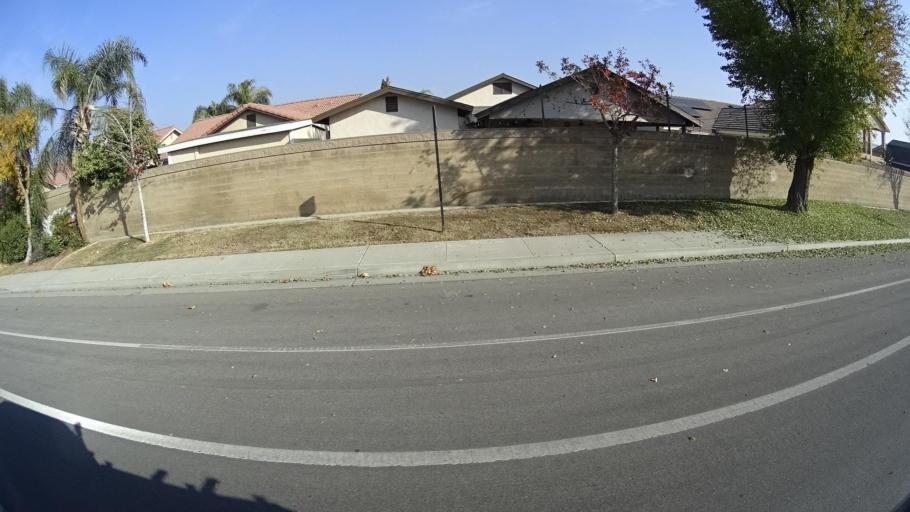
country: US
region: California
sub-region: Kern County
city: Delano
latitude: 35.7867
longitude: -119.2244
